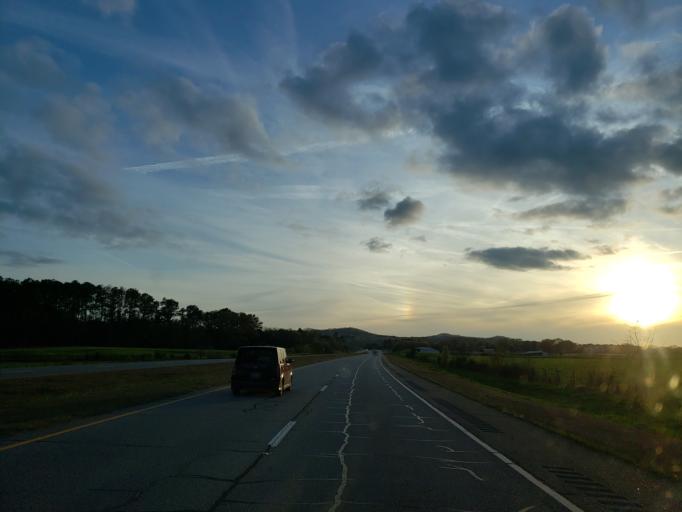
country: US
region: Georgia
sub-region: Bartow County
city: Euharlee
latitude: 34.0850
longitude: -84.9708
